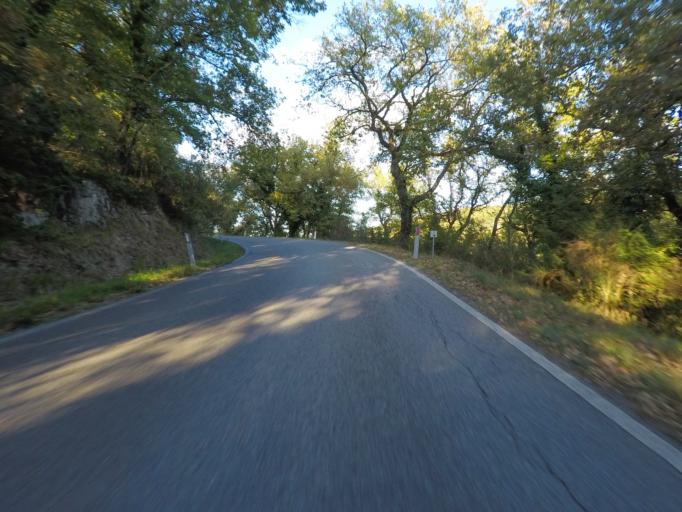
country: IT
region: Tuscany
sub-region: Provincia di Siena
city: Radda in Chianti
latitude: 43.4746
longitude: 11.3737
